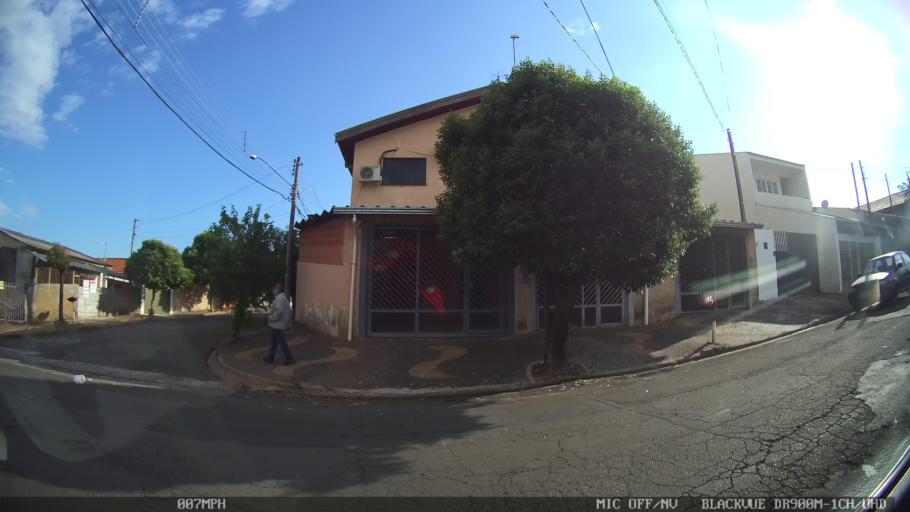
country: BR
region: Sao Paulo
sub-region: Americana
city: Americana
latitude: -22.7276
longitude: -47.3681
